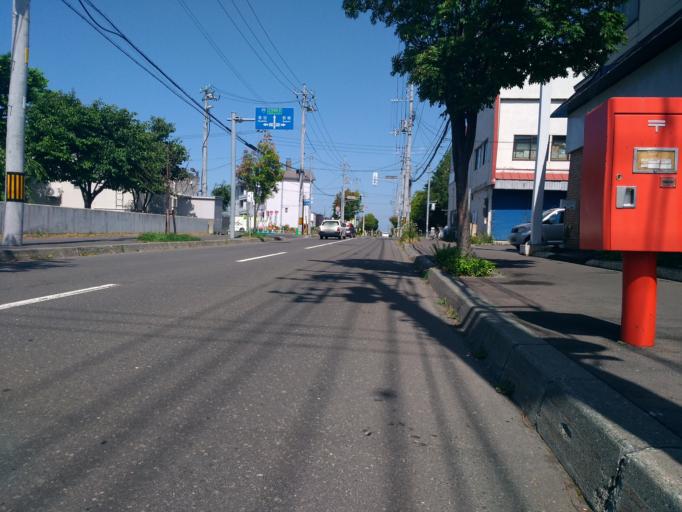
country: JP
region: Hokkaido
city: Ebetsu
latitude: 43.0785
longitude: 141.4977
